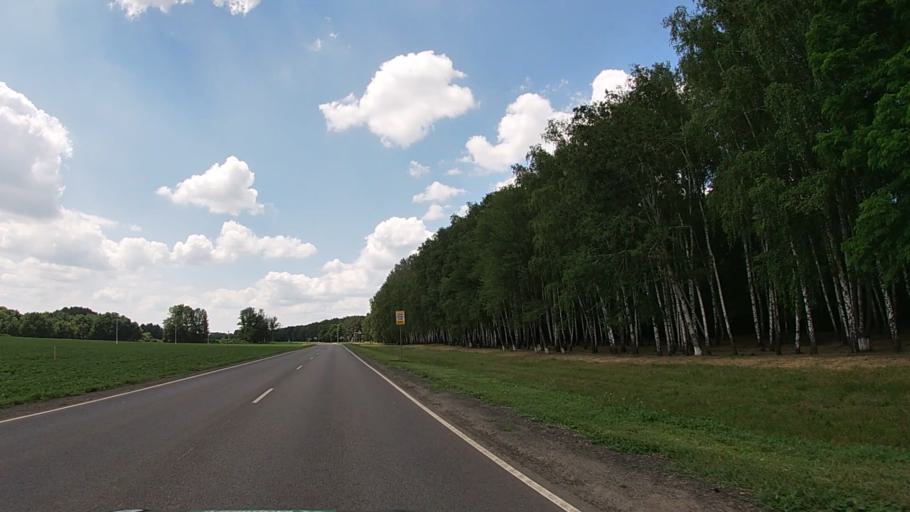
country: RU
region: Belgorod
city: Grayvoron
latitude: 50.5015
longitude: 35.7273
